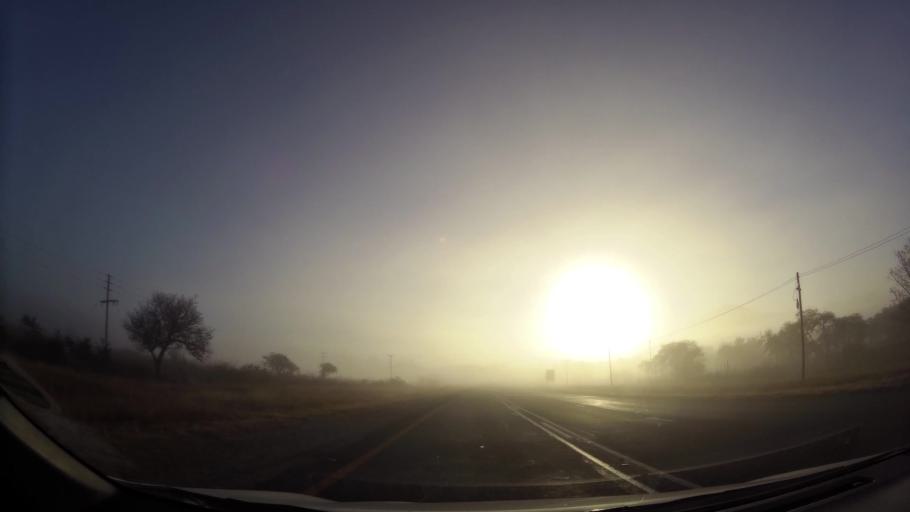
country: ZA
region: Limpopo
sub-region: Capricorn District Municipality
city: Polokwane
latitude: -24.0335
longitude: 29.2851
